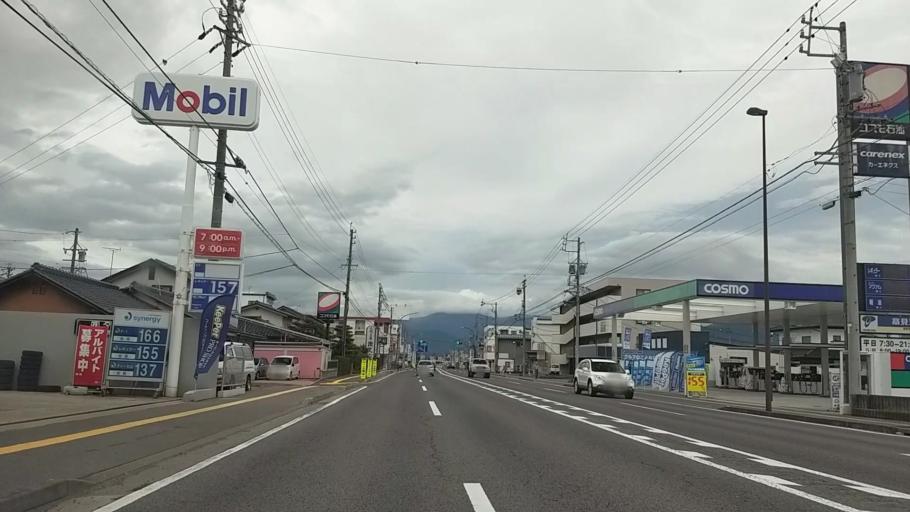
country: JP
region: Nagano
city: Nagano-shi
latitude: 36.6480
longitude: 138.2094
